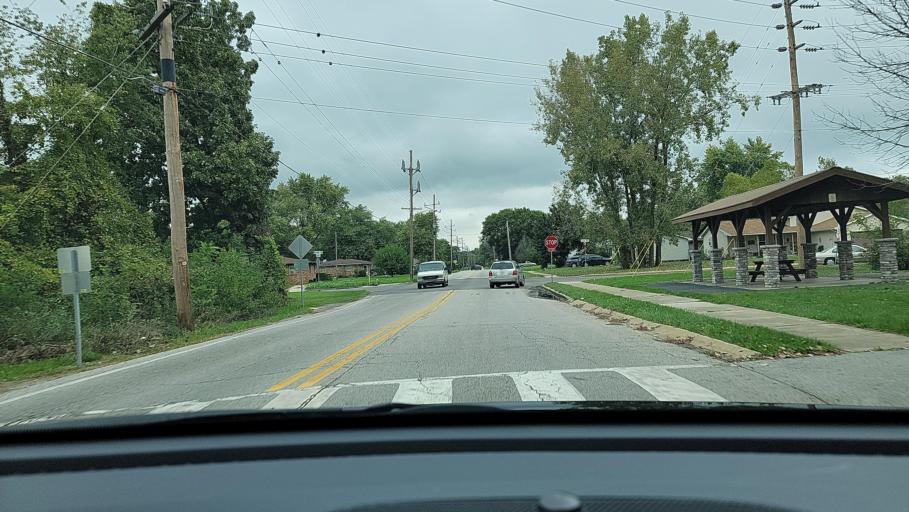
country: US
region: Indiana
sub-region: Porter County
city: Portage
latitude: 41.5574
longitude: -87.1973
